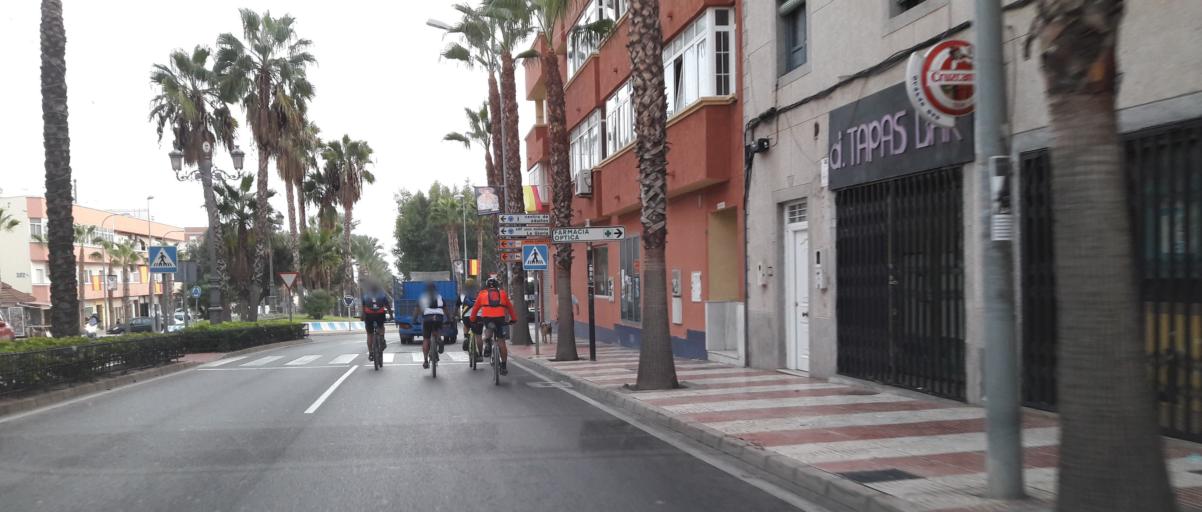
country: ES
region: Andalusia
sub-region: Provincia de Almeria
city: Aguadulce
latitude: 36.8071
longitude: -2.5984
